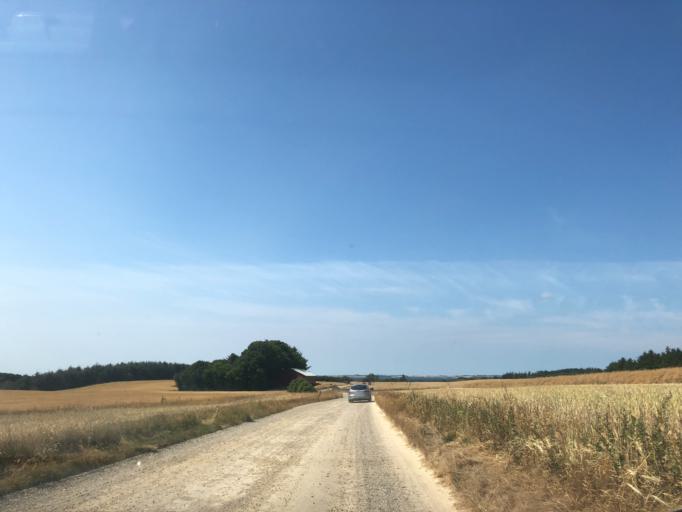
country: DK
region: North Denmark
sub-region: Morso Kommune
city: Nykobing Mors
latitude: 56.8252
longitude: 8.9770
